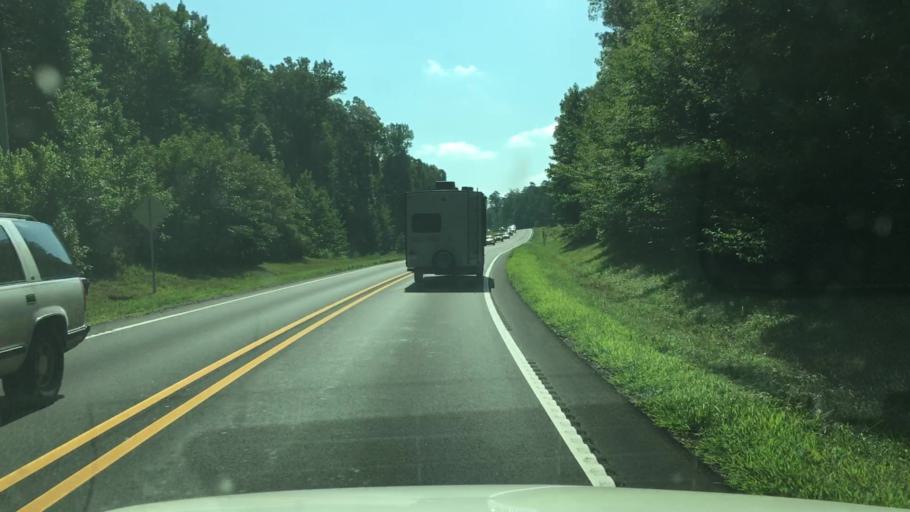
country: US
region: Arkansas
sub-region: Garland County
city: Rockwell
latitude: 34.5233
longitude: -93.3301
